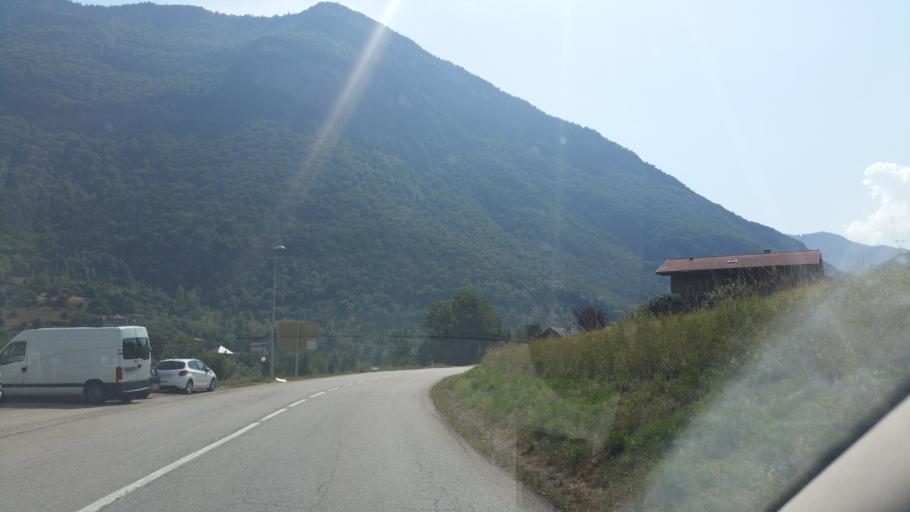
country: FR
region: Rhone-Alpes
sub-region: Departement de la Savoie
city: Aigueblanche
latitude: 45.5012
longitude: 6.5028
